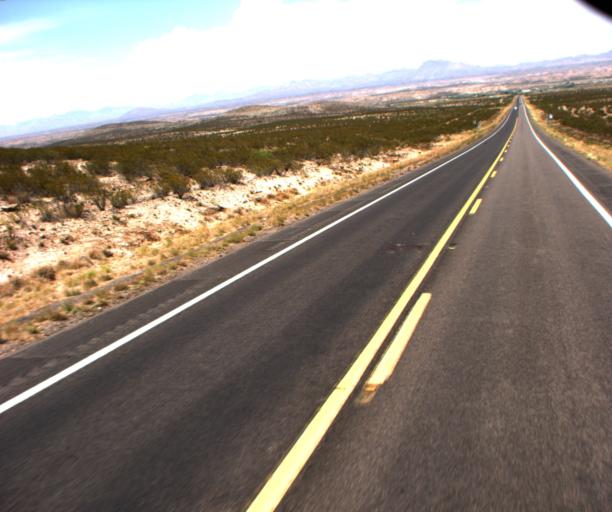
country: US
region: Arizona
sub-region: Greenlee County
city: Clifton
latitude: 32.7289
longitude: -109.1586
